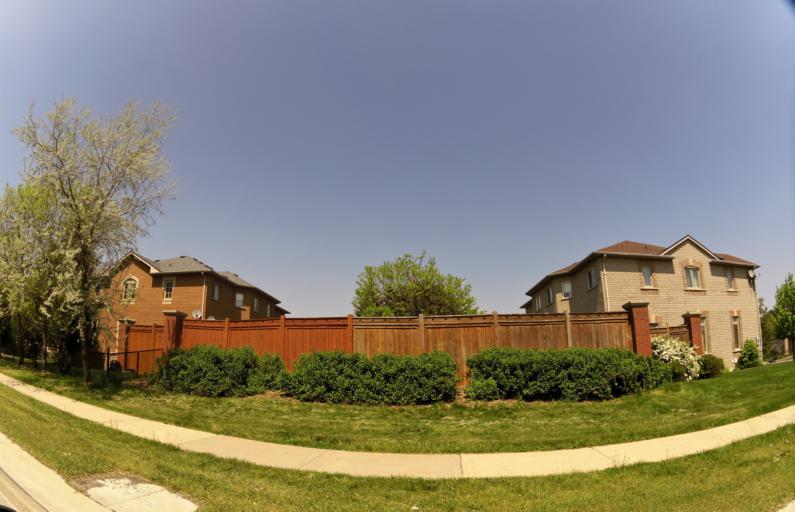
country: CA
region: Ontario
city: Mississauga
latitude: 43.6191
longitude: -79.6456
